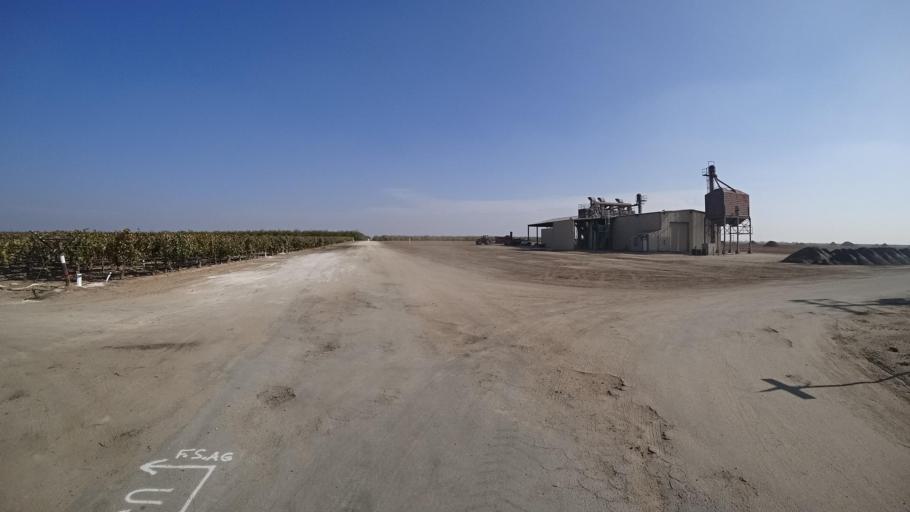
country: US
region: California
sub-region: Kern County
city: Shafter
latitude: 35.5442
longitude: -119.1335
